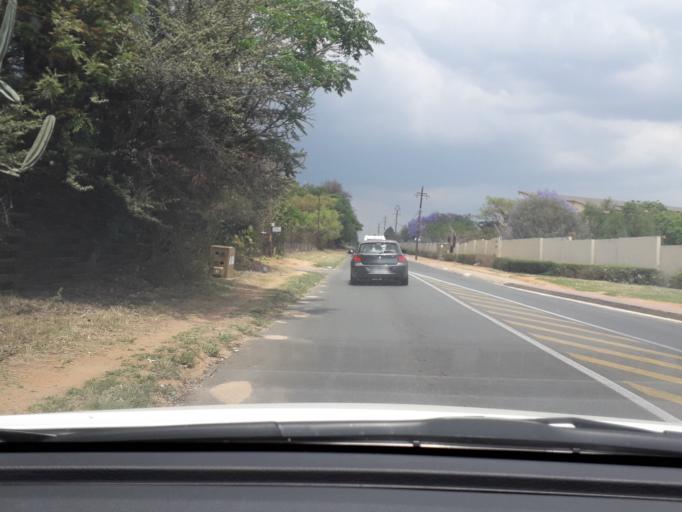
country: ZA
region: Gauteng
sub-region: West Rand District Municipality
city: Muldersdriseloop
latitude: -26.0586
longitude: 27.9269
